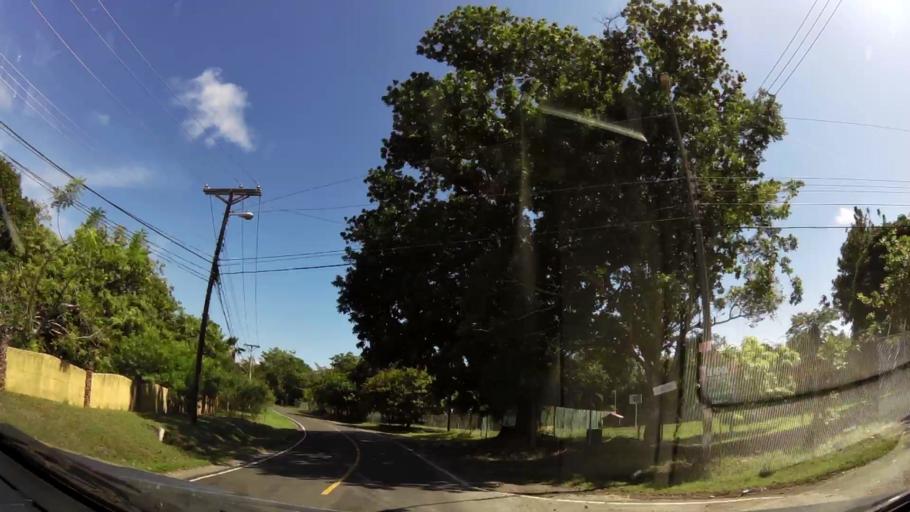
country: PA
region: Panama
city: Nueva Gorgona
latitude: 8.5589
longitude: -79.8869
